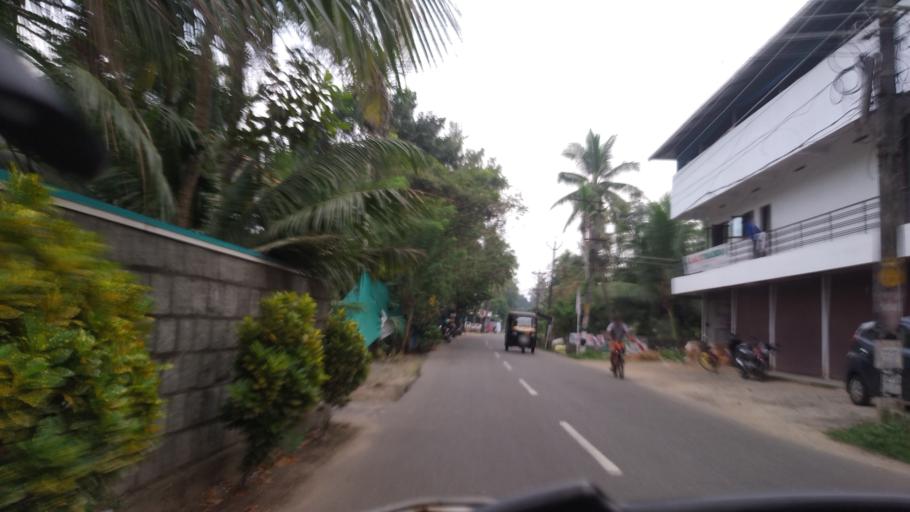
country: IN
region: Kerala
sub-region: Ernakulam
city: Elur
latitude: 10.1376
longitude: 76.2468
